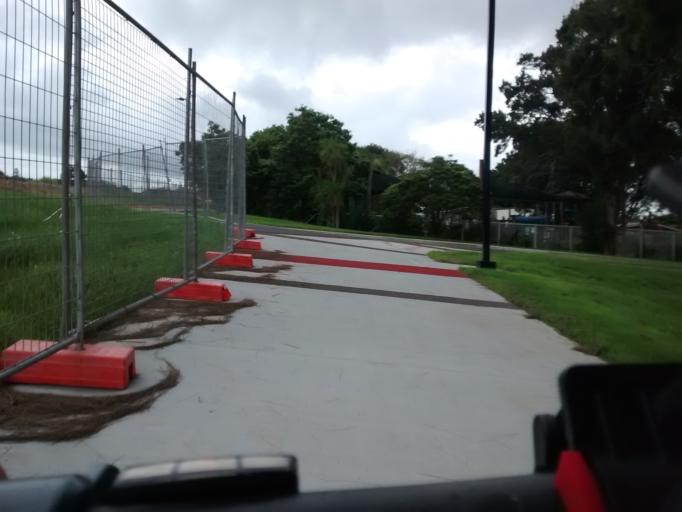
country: NZ
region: Auckland
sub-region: Auckland
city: Rosebank
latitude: -36.8851
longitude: 174.7041
